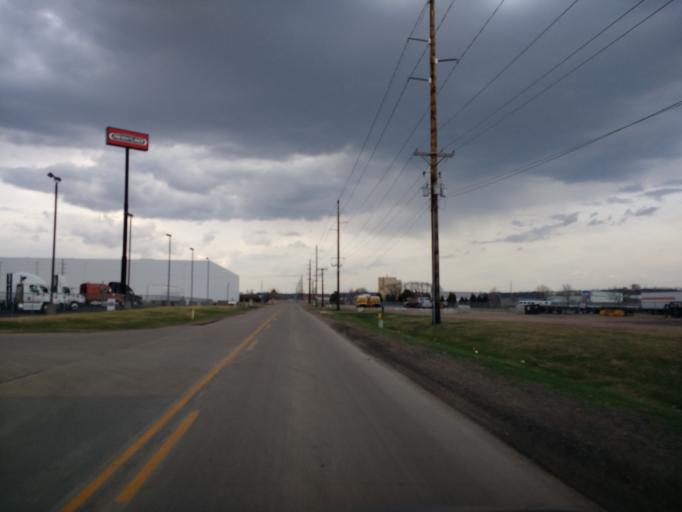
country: US
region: Iowa
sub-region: Woodbury County
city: Sergeant Bluff
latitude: 42.4232
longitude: -96.3698
